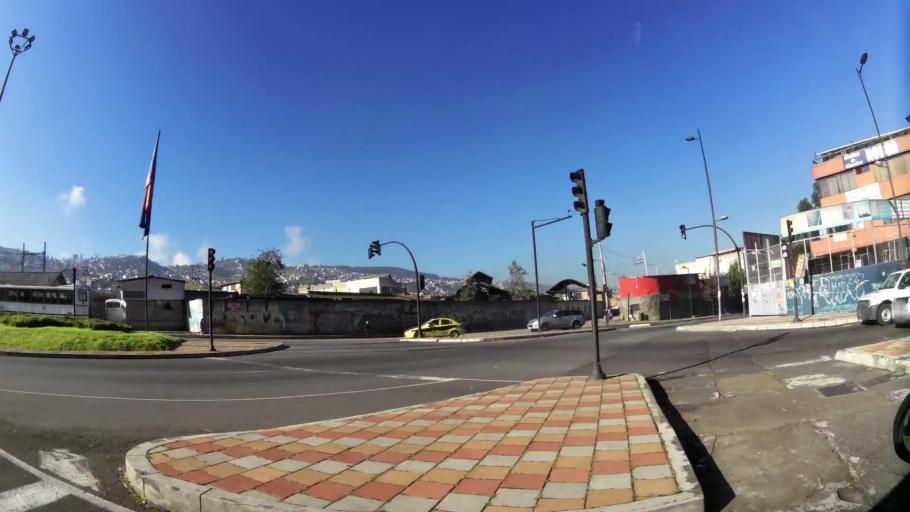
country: EC
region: Pichincha
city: Quito
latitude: -0.2458
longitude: -78.5164
